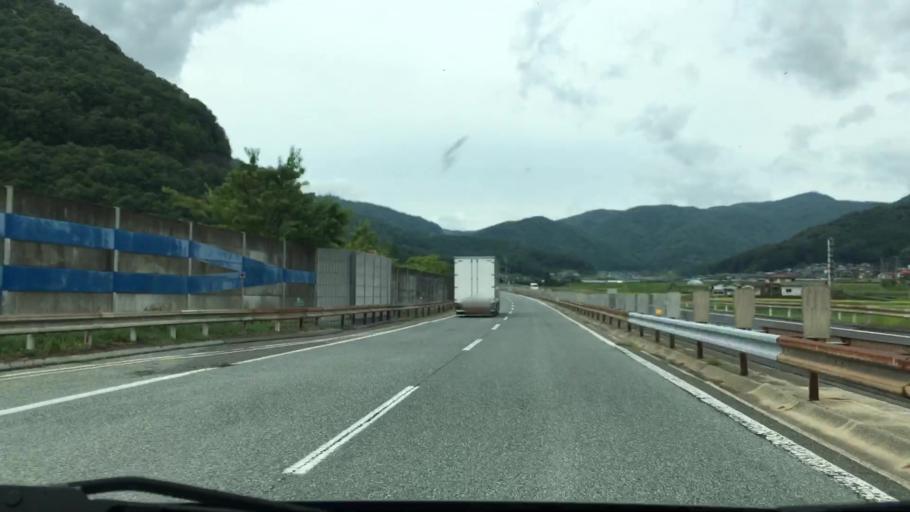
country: JP
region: Okayama
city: Niimi
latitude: 34.9686
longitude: 133.6276
